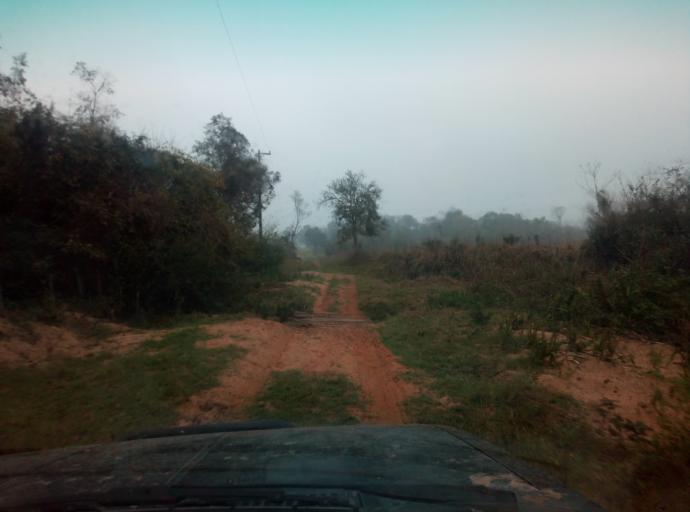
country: PY
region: Caaguazu
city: Doctor Cecilio Baez
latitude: -25.1554
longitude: -56.2612
